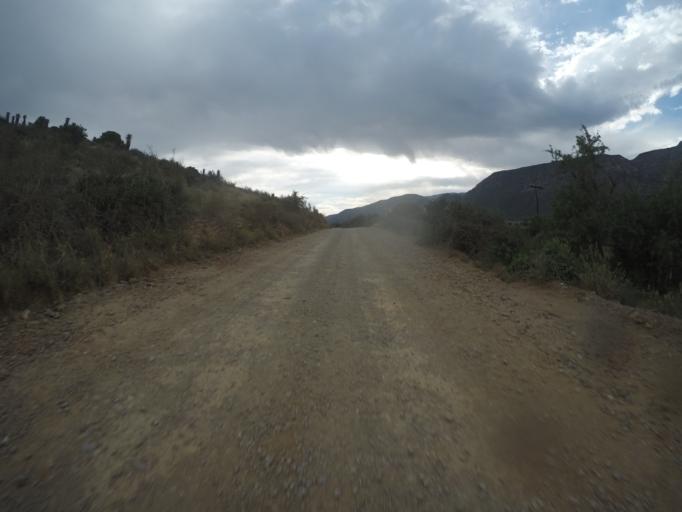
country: ZA
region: Eastern Cape
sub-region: Cacadu District Municipality
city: Willowmore
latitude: -33.5274
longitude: 23.8598
